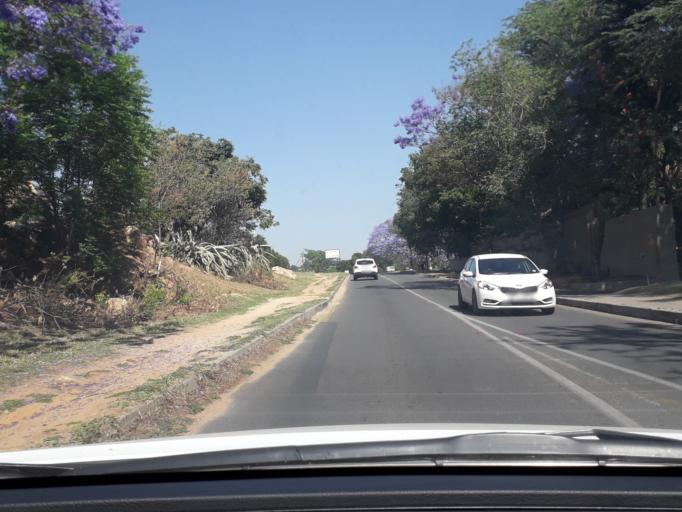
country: ZA
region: Gauteng
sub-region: City of Johannesburg Metropolitan Municipality
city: Roodepoort
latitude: -26.0833
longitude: 27.9561
